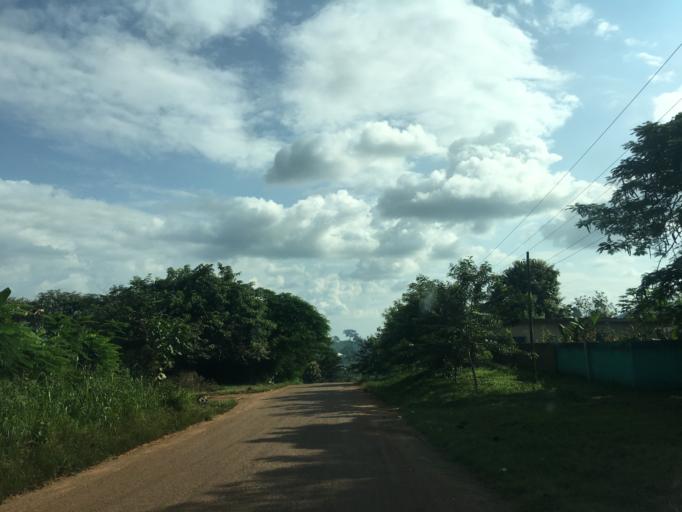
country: GH
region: Western
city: Bibiani
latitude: 6.7981
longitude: -2.5256
